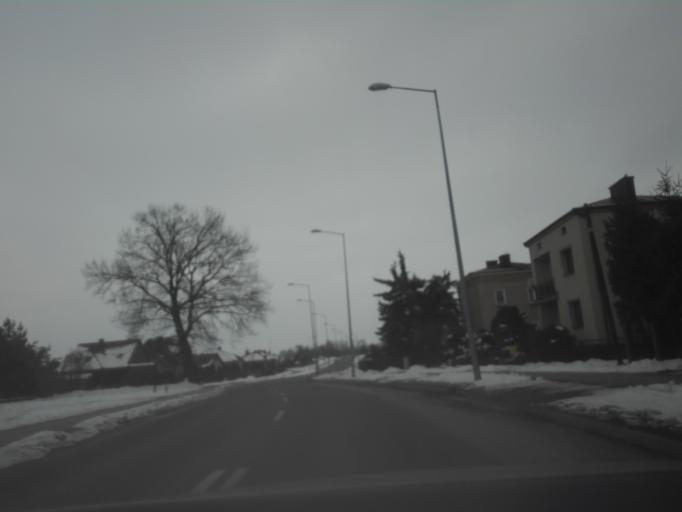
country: PL
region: Lublin Voivodeship
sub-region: Powiat hrubieszowski
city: Hrubieszow
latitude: 50.7996
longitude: 23.8965
